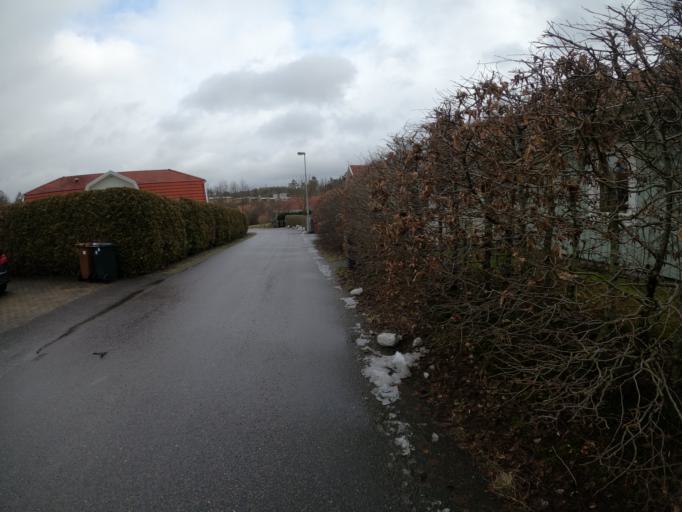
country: SE
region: Vaestra Goetaland
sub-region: Harryda Kommun
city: Molnlycke
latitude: 57.6421
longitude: 12.1075
